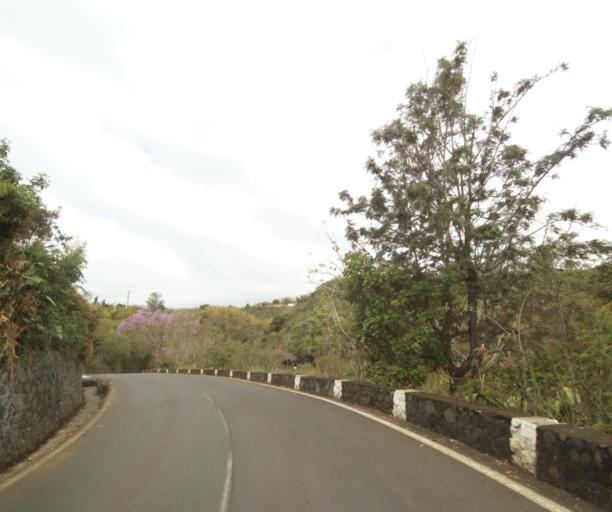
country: RE
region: Reunion
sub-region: Reunion
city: Saint-Paul
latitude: -21.0456
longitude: 55.2877
